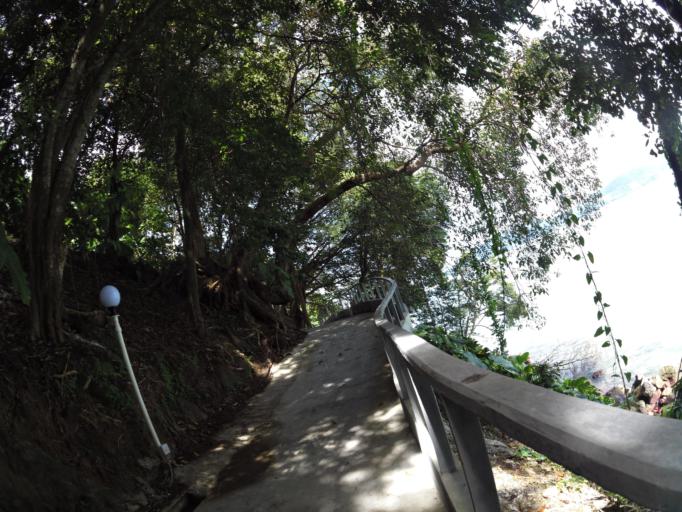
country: TH
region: Phuket
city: Patong
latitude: 7.8872
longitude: 98.2824
